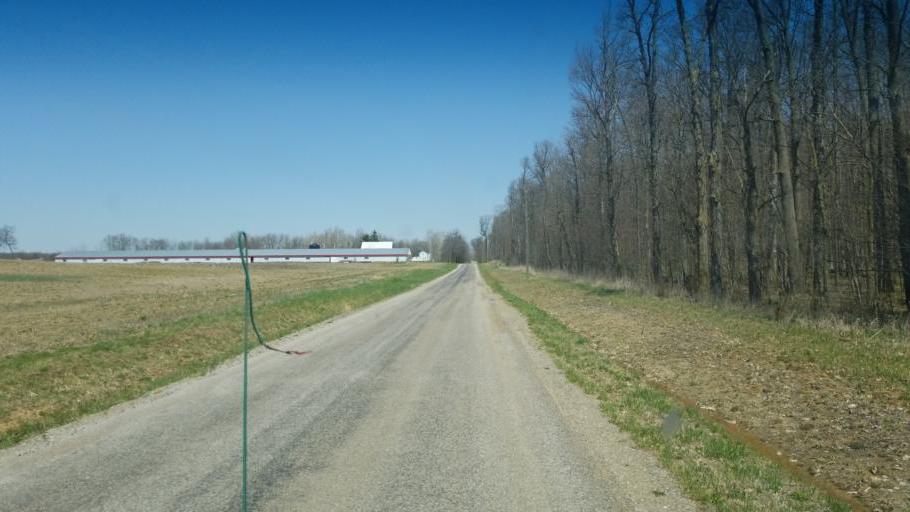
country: US
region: Ohio
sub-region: Huron County
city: New London
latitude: 41.0203
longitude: -82.4343
